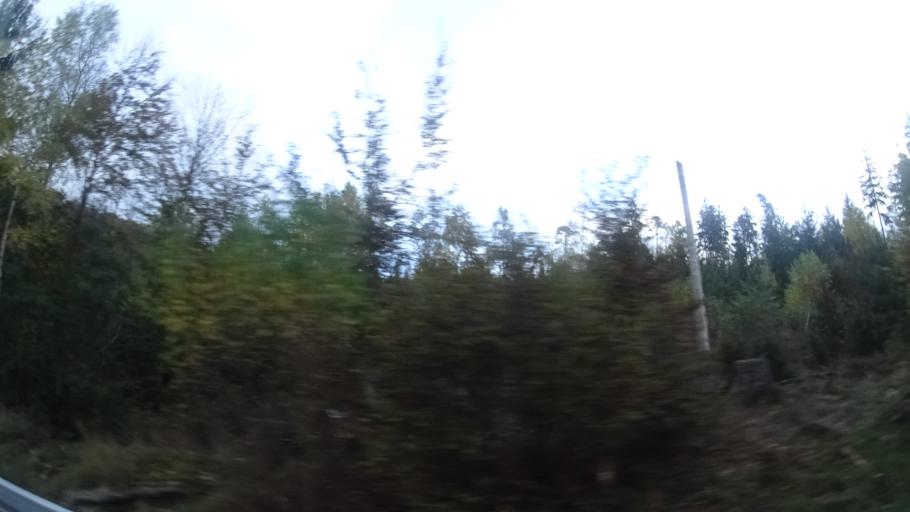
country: DE
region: Hesse
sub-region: Regierungsbezirk Kassel
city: Hosenfeld
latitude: 50.4658
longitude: 9.5162
